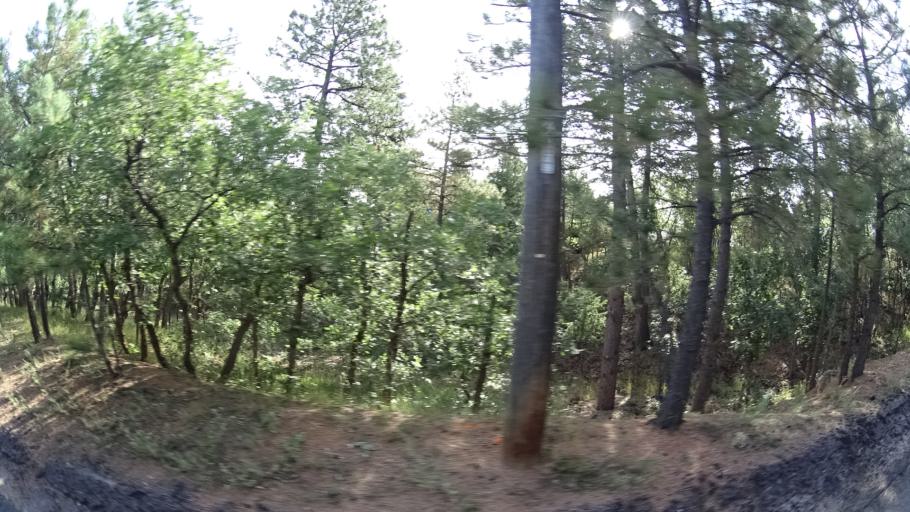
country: US
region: Colorado
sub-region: El Paso County
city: Colorado Springs
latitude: 38.8105
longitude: -104.8733
